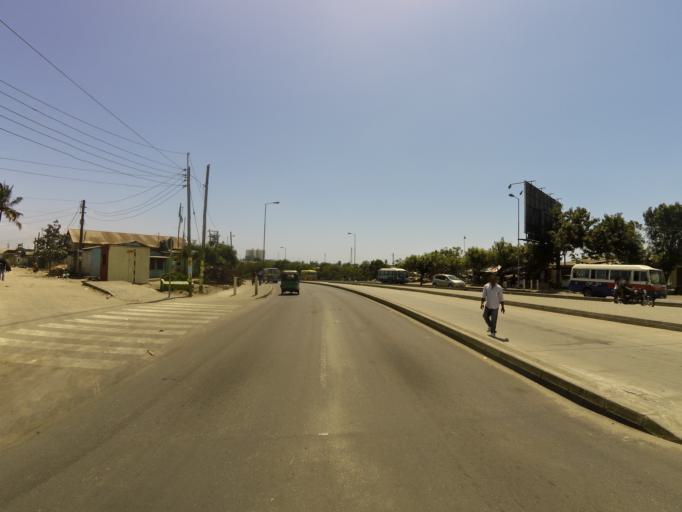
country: TZ
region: Dar es Salaam
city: Magomeni
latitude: -6.8038
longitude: 39.2608
